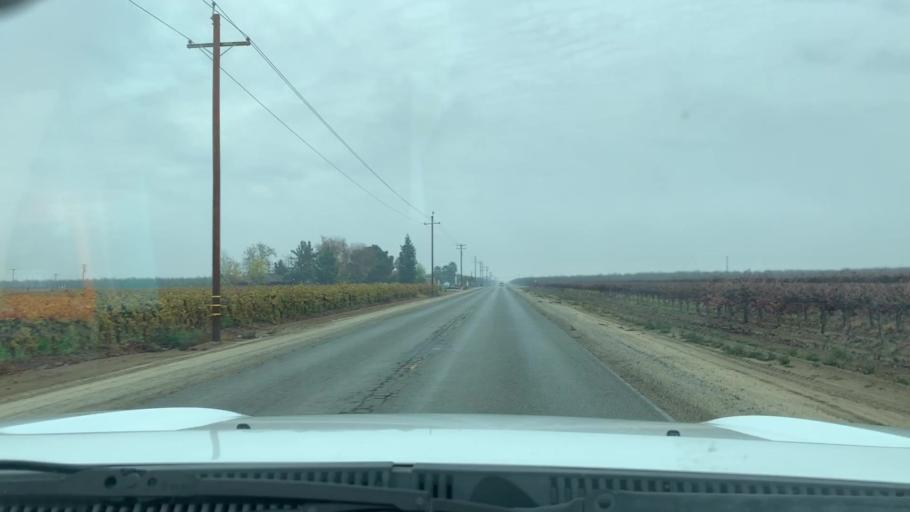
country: US
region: California
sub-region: Kern County
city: Delano
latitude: 35.7611
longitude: -119.3687
